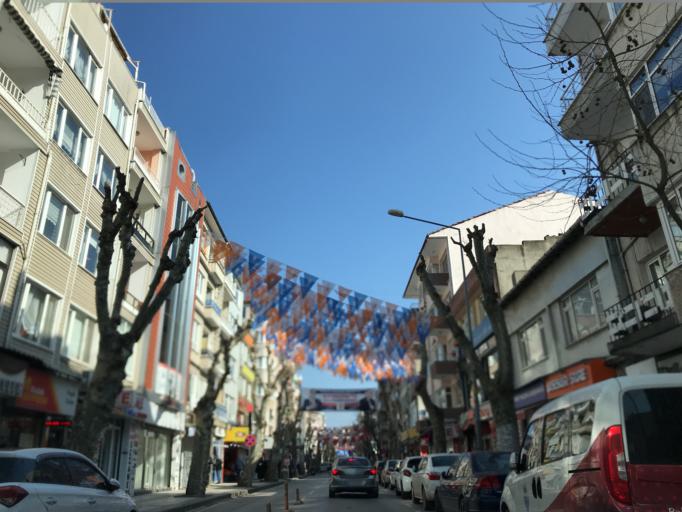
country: TR
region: Yalova
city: Yalova
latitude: 40.6558
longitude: 29.2699
